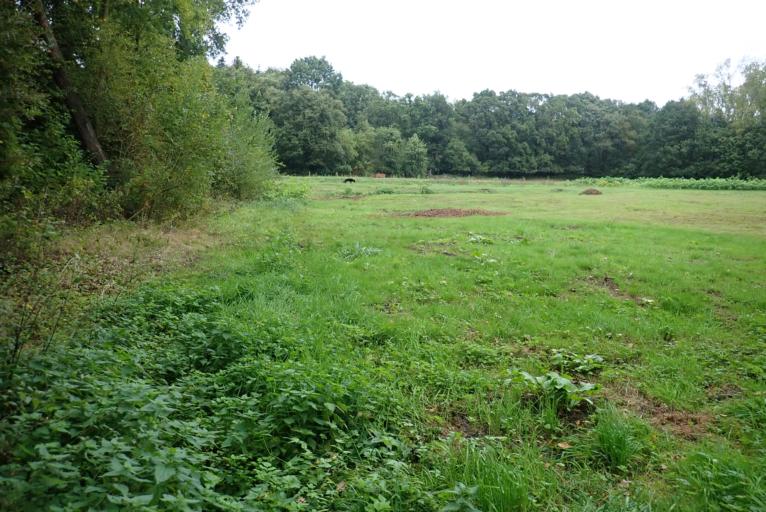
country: BE
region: Flanders
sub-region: Provincie Antwerpen
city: Hulshout
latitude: 51.0642
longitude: 4.8186
